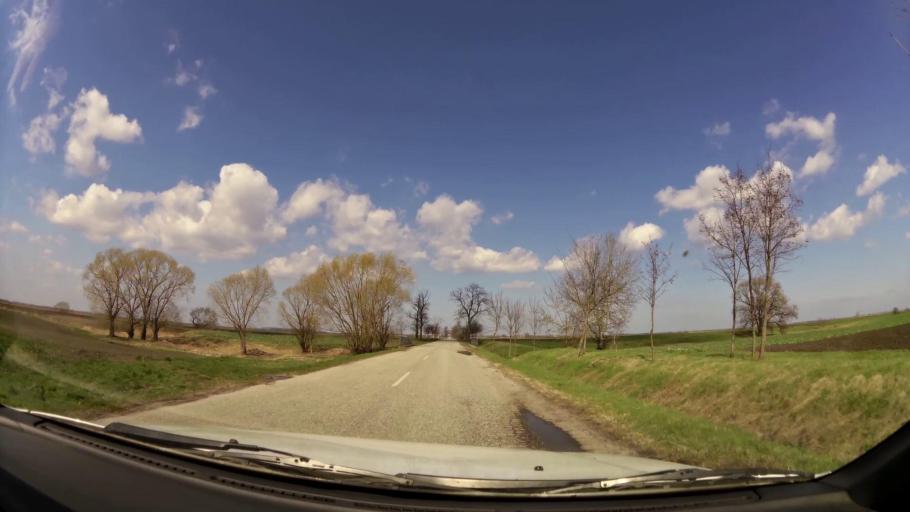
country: HU
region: Pest
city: Ujszilvas
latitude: 47.3040
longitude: 19.9404
